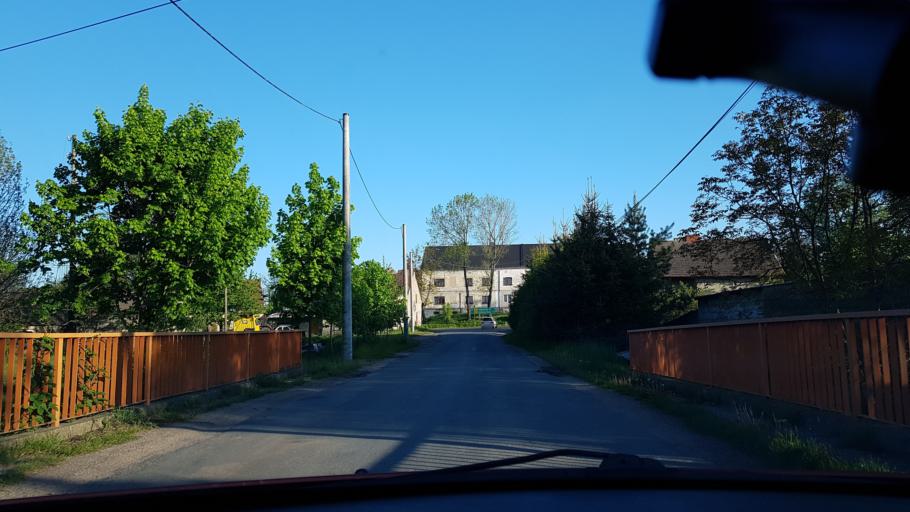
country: PL
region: Lower Silesian Voivodeship
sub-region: Powiat zabkowicki
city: Stoszowice
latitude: 50.6004
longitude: 16.7381
